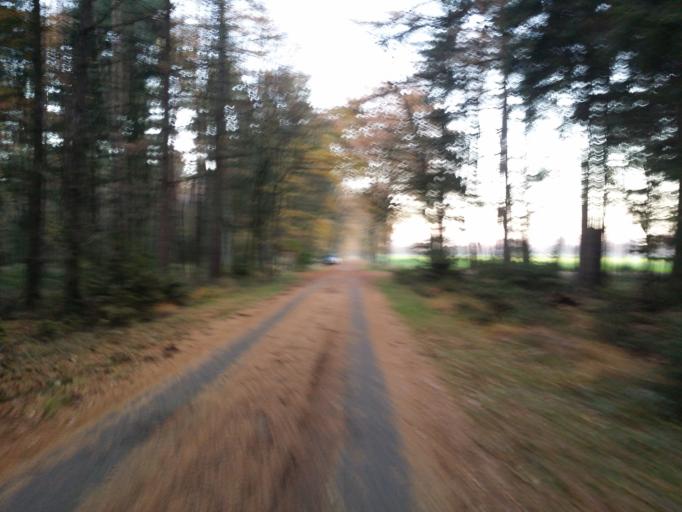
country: DE
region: Lower Saxony
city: Ahausen
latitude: 53.0969
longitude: 9.3162
